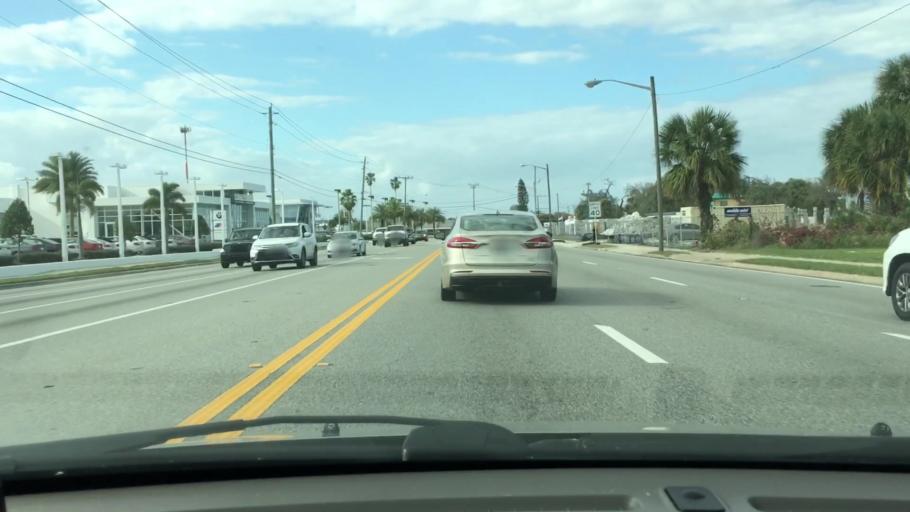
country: US
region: Florida
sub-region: Brevard County
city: Melbourne
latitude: 28.0855
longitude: -80.6063
